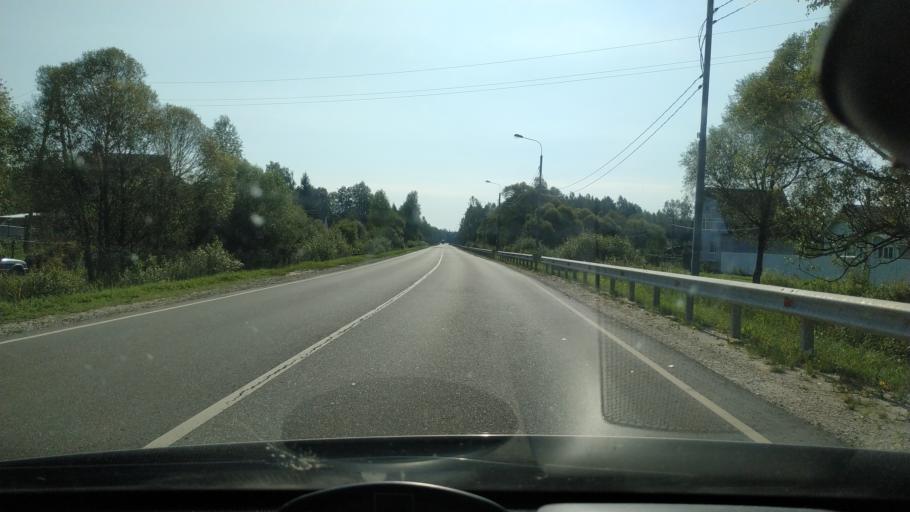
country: RU
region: Moskovskaya
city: Dmitrovskiy Pogost
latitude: 55.2322
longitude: 39.9125
